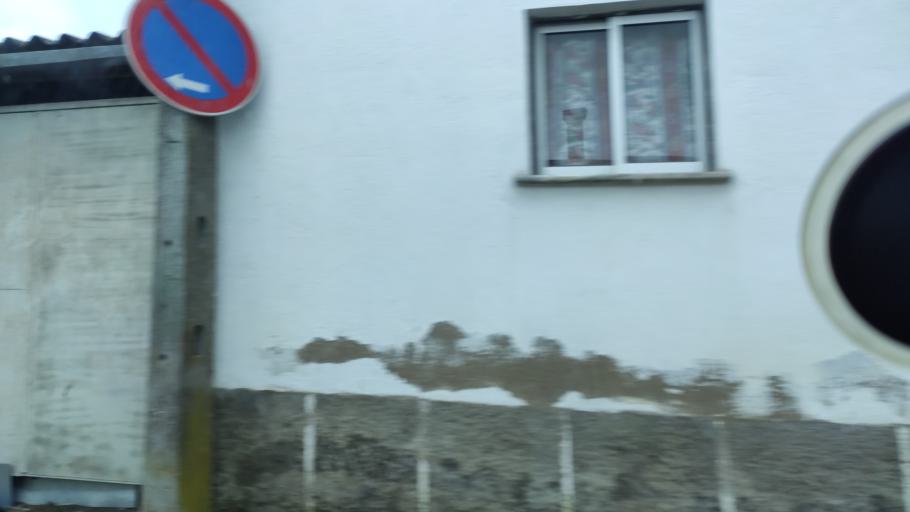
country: PT
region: Beja
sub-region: Beja
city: Beja
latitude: 38.0144
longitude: -7.8509
